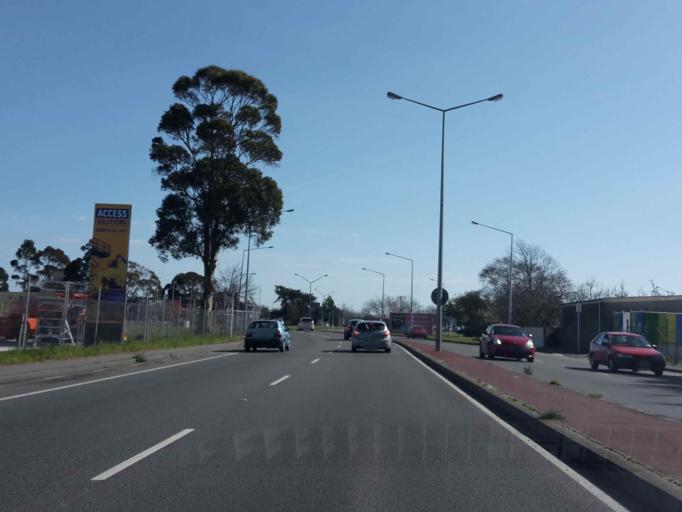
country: NZ
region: Canterbury
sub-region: Selwyn District
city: Prebbleton
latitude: -43.5392
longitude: 172.5566
